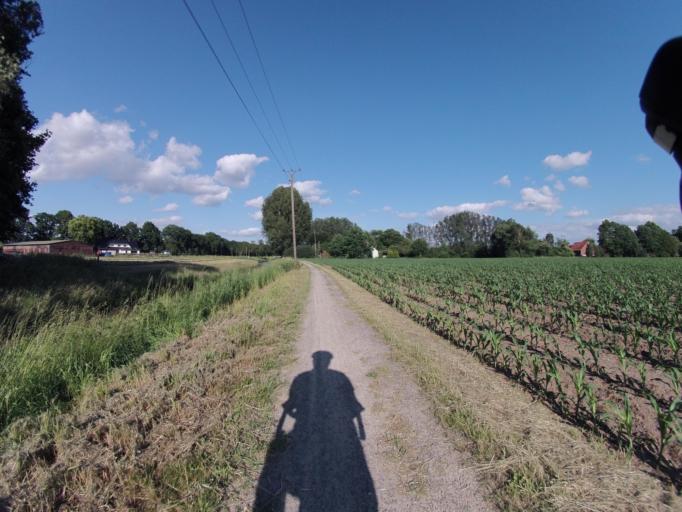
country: DE
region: North Rhine-Westphalia
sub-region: Regierungsbezirk Munster
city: Horstel
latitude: 52.2947
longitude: 7.6060
